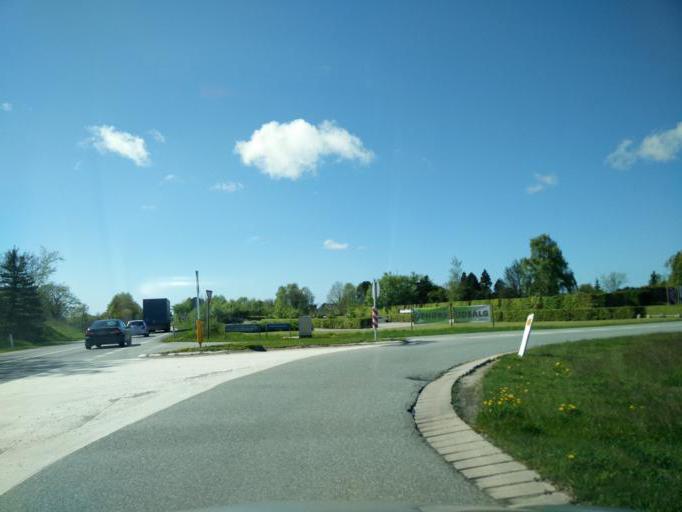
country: DK
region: Capital Region
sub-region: Gribskov Kommune
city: Helsinge
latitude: 56.0090
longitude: 12.2184
